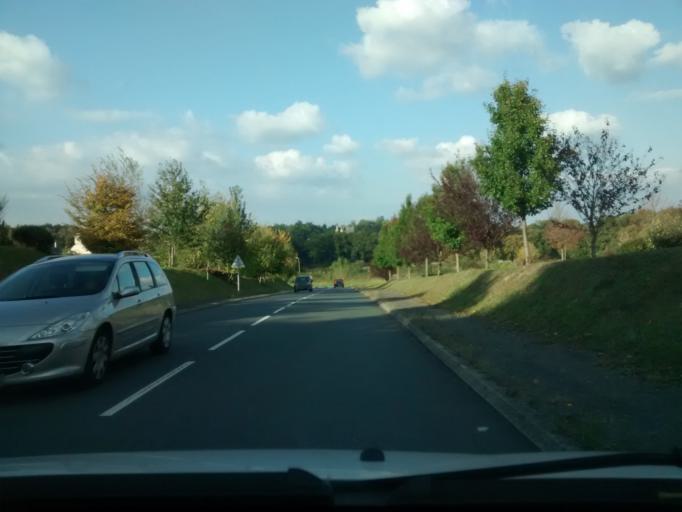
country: FR
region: Pays de la Loire
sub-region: Departement de la Loire-Atlantique
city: Orvault
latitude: 47.2705
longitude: -1.6143
